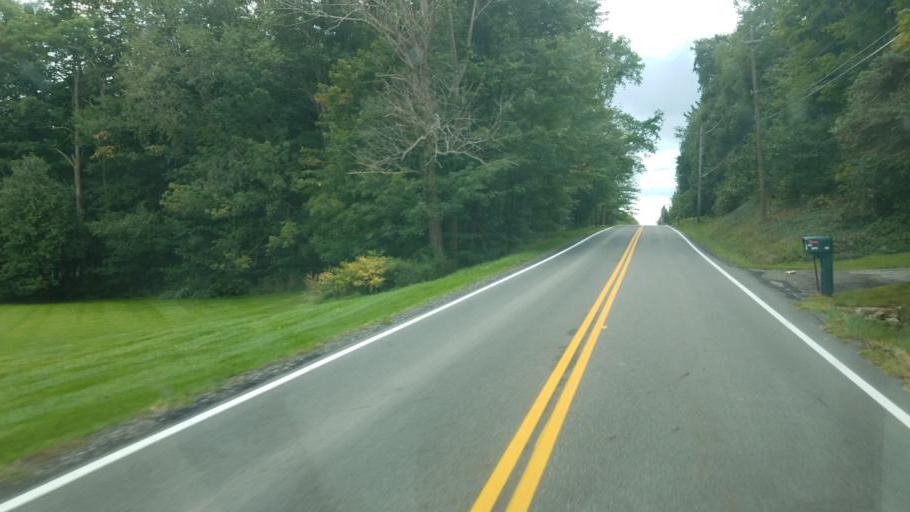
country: US
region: Ohio
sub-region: Geauga County
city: Burton
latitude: 41.5200
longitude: -81.1803
